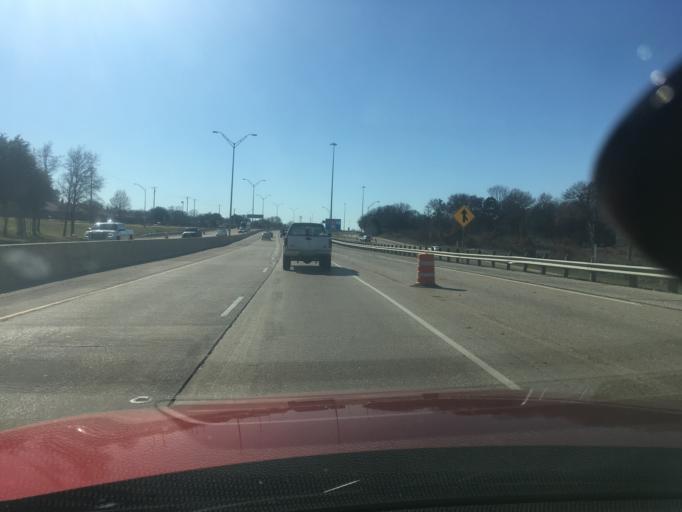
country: US
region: Texas
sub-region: Dallas County
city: Cockrell Hill
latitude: 32.6895
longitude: -96.8471
